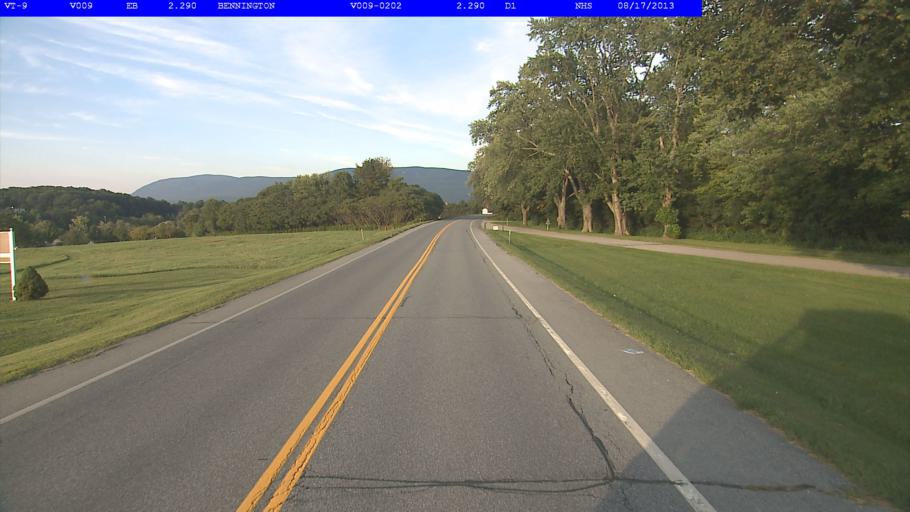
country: US
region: Vermont
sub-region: Bennington County
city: Bennington
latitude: 42.8808
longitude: -73.2342
